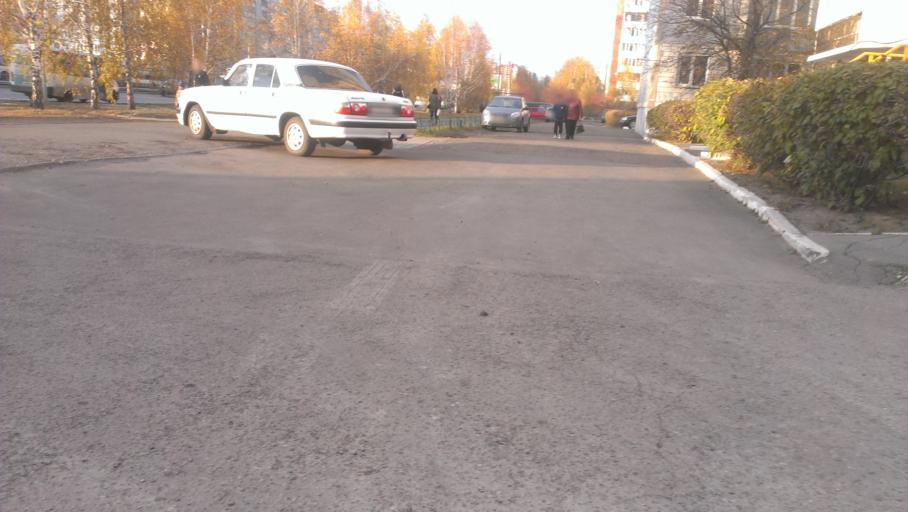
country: RU
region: Altai Krai
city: Novosilikatnyy
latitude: 53.3384
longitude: 83.6703
